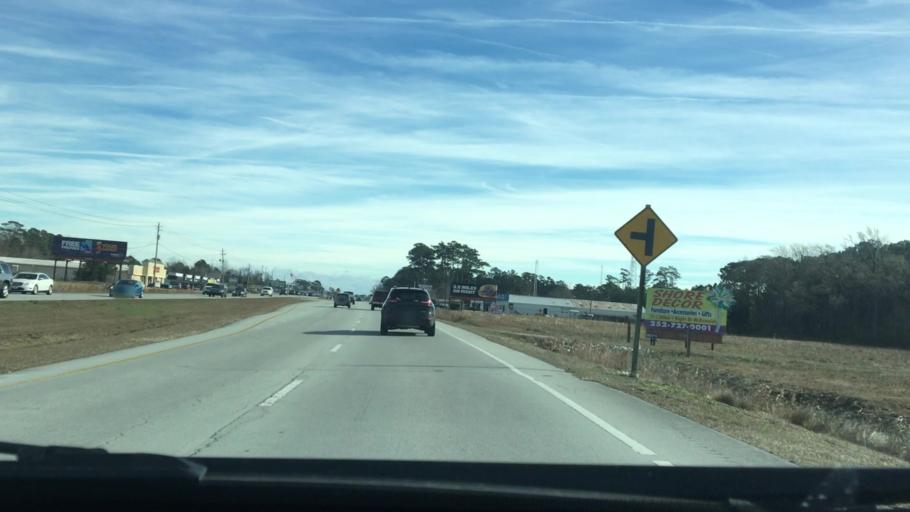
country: US
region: North Carolina
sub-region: Carteret County
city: Newport
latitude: 34.7456
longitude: -76.8321
